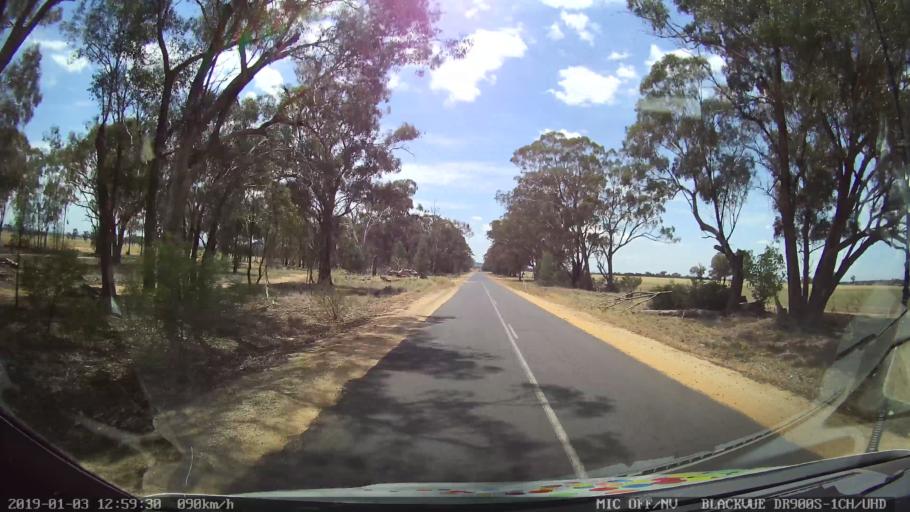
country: AU
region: New South Wales
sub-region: Cabonne
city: Canowindra
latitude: -33.6364
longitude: 148.3901
